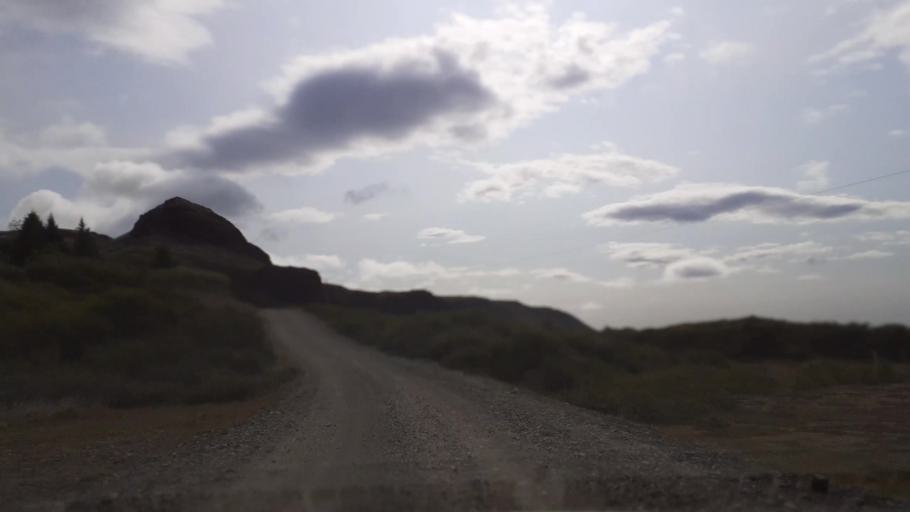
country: IS
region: East
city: Hoefn
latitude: 64.4358
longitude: -14.9006
